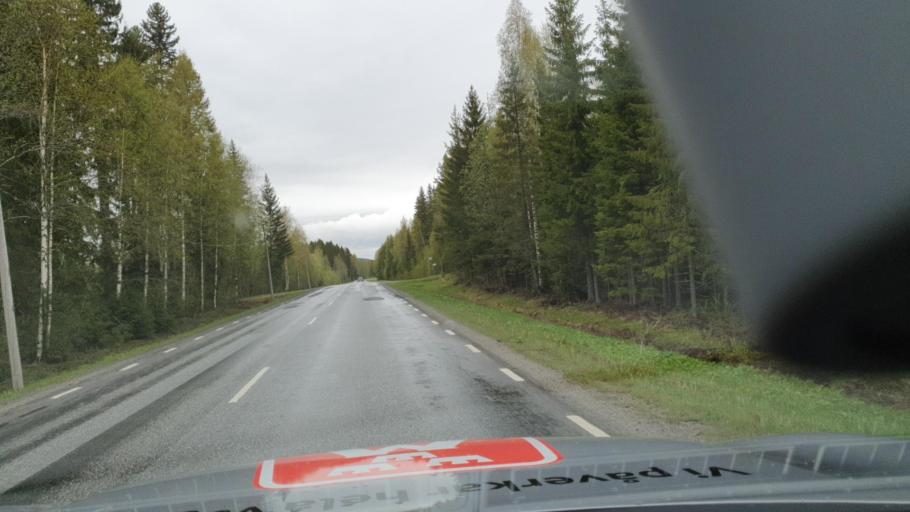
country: SE
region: Vaesternorrland
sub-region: OErnskoeldsviks Kommun
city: Bjasta
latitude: 63.4111
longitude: 18.4425
